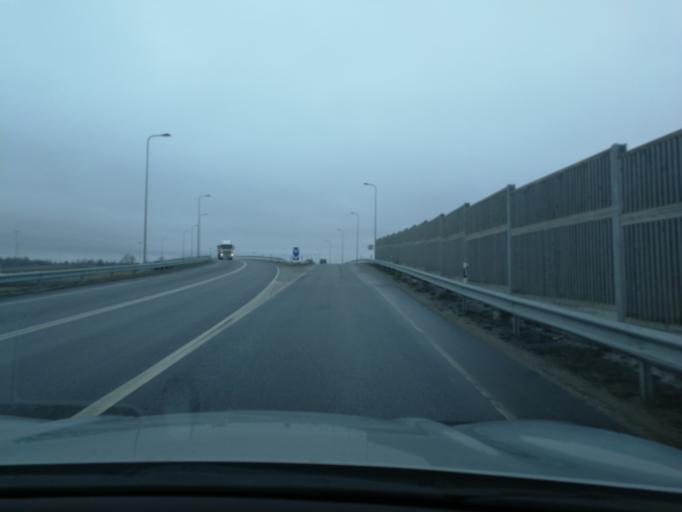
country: EE
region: Harju
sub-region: Raasiku vald
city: Arukula
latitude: 59.1840
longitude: 25.1276
